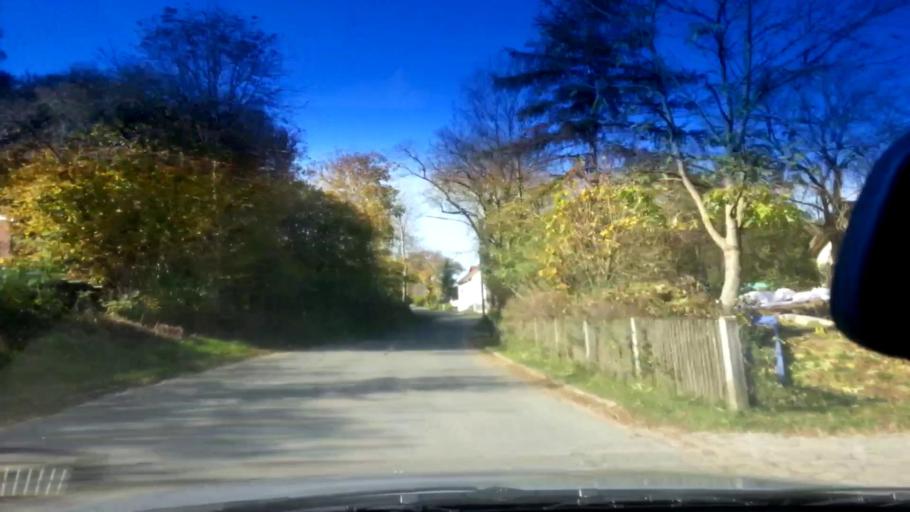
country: DE
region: Bavaria
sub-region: Upper Franconia
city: Wonsees
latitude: 49.9768
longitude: 11.2978
